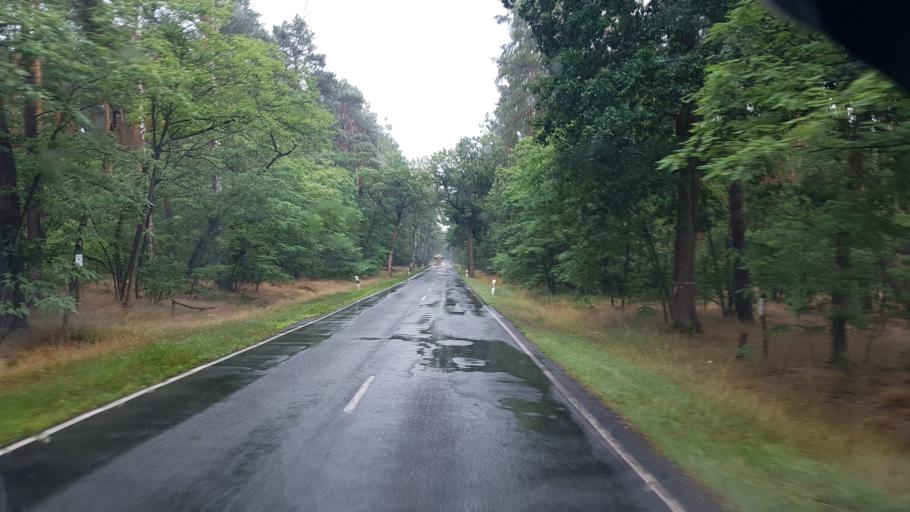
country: DE
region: Brandenburg
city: Lebusa
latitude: 51.8289
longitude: 13.4162
